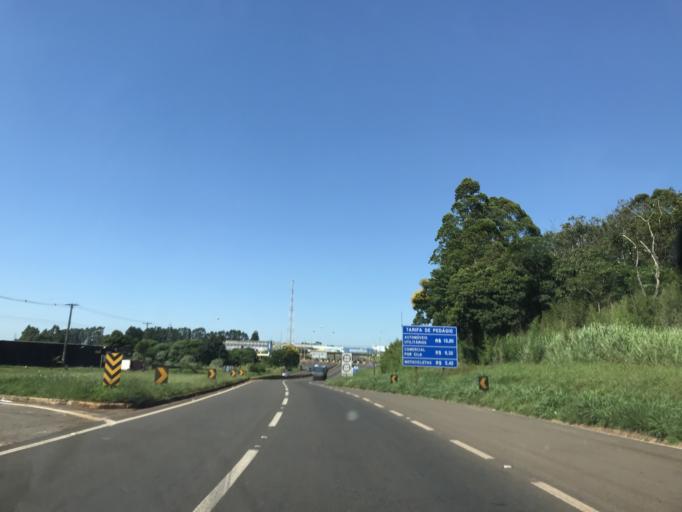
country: BR
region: Parana
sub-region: Rolandia
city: Rolandia
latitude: -23.3577
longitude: -51.3960
